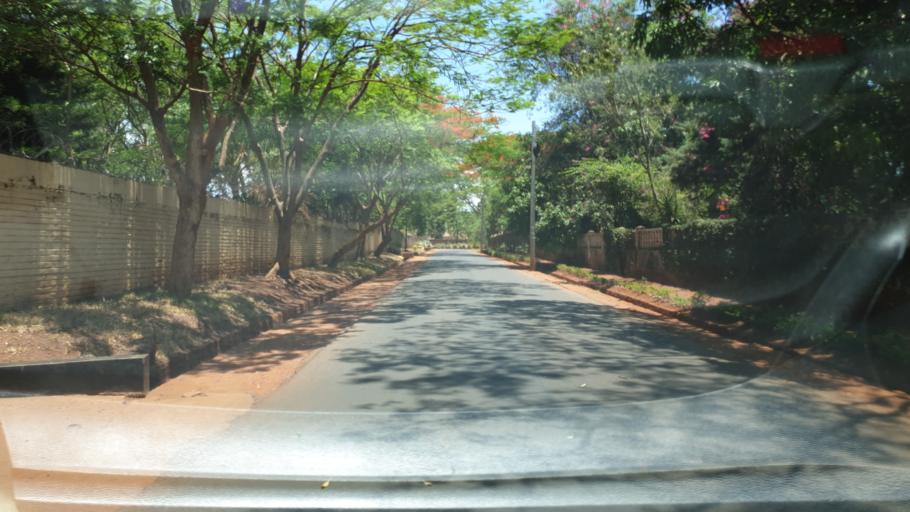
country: MW
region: Central Region
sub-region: Lilongwe District
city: Lilongwe
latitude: -13.9843
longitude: 33.7550
